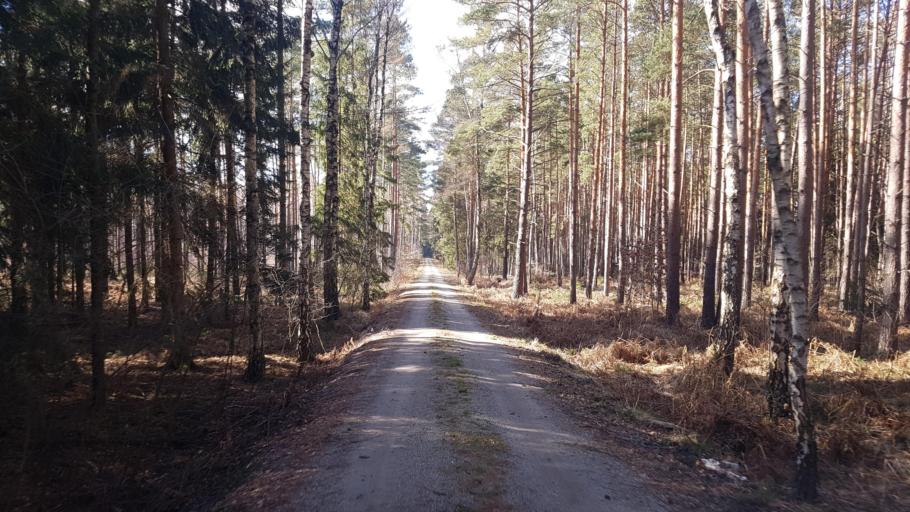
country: DE
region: Brandenburg
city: Plessa
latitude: 51.5162
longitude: 13.6045
